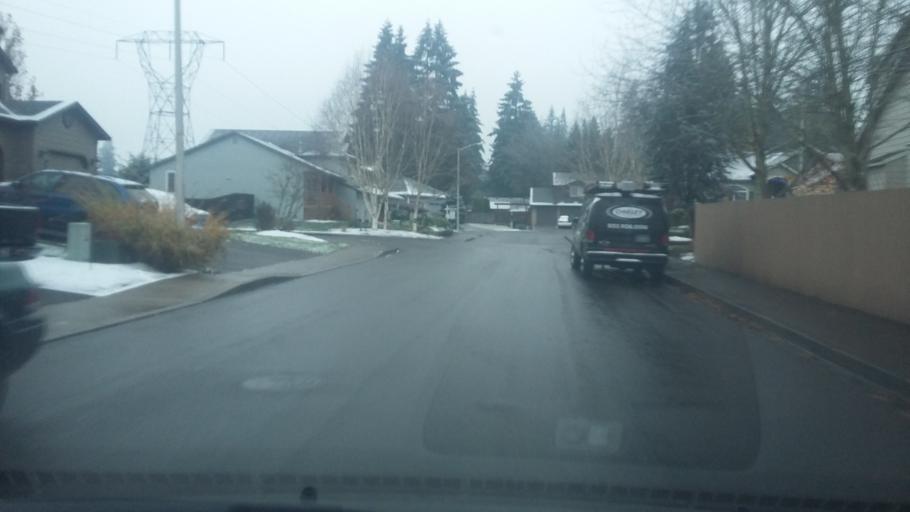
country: US
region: Washington
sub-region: Clark County
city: Salmon Creek
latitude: 45.7016
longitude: -122.6323
